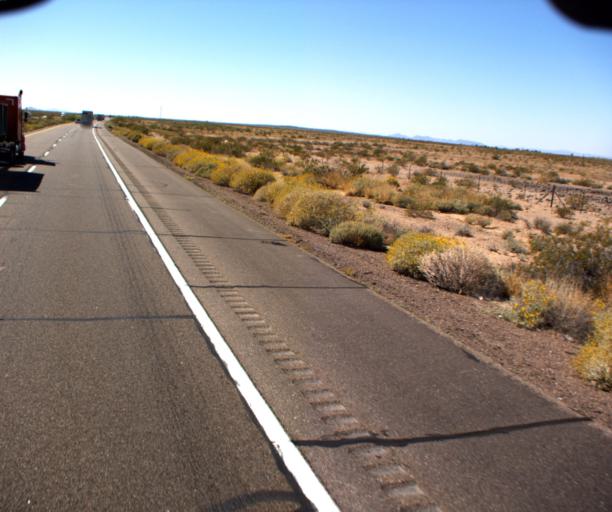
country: US
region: Arizona
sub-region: Maricopa County
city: Gila Bend
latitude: 32.8629
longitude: -113.1707
